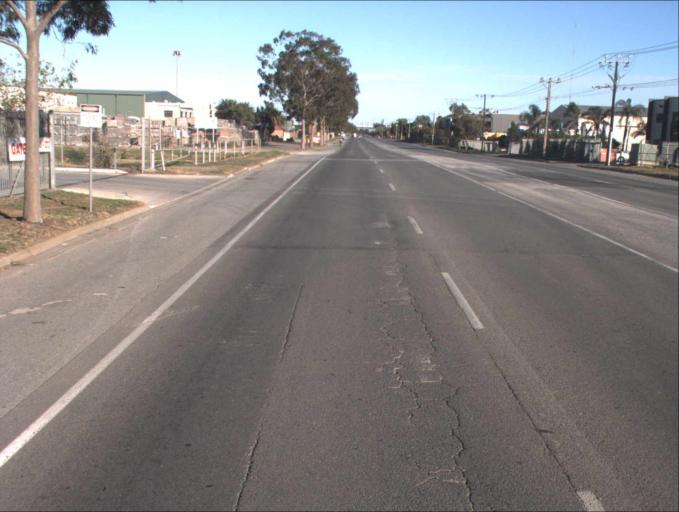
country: AU
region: South Australia
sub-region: Port Adelaide Enfield
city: Blair Athol
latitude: -34.8400
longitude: 138.5773
